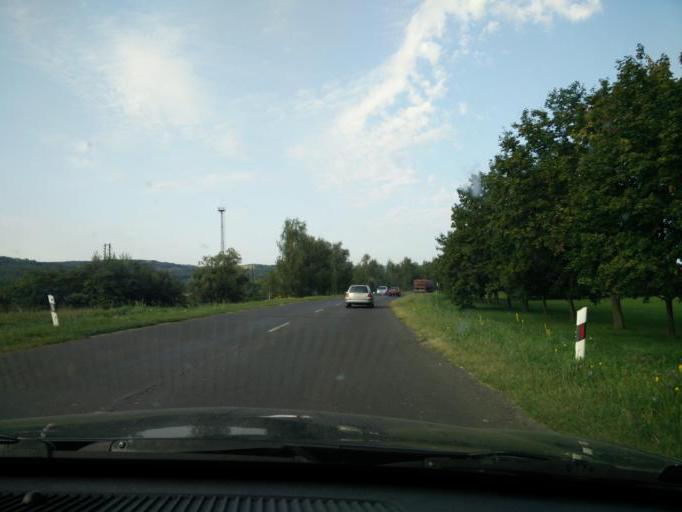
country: HU
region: Tolna
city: Nagymanyok
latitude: 46.2829
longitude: 18.4655
